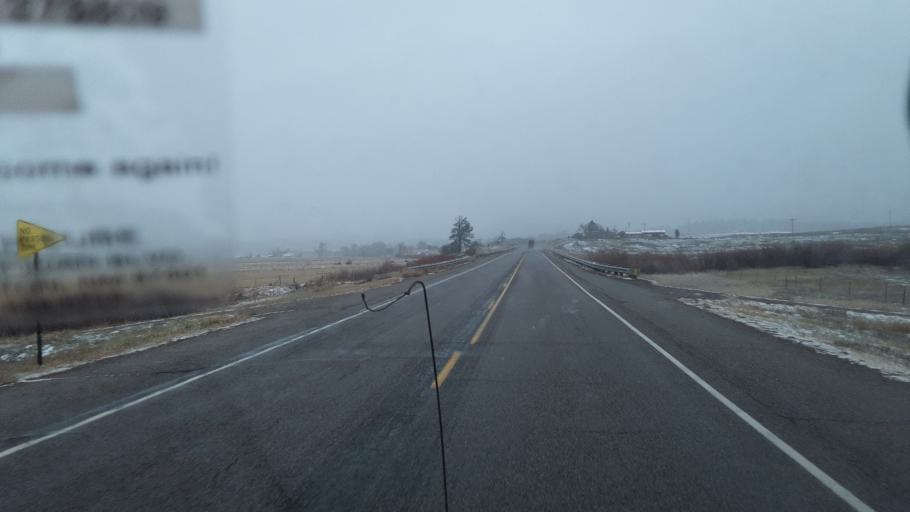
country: US
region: New Mexico
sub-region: Rio Arriba County
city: Tierra Amarilla
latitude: 36.7531
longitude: -106.5627
